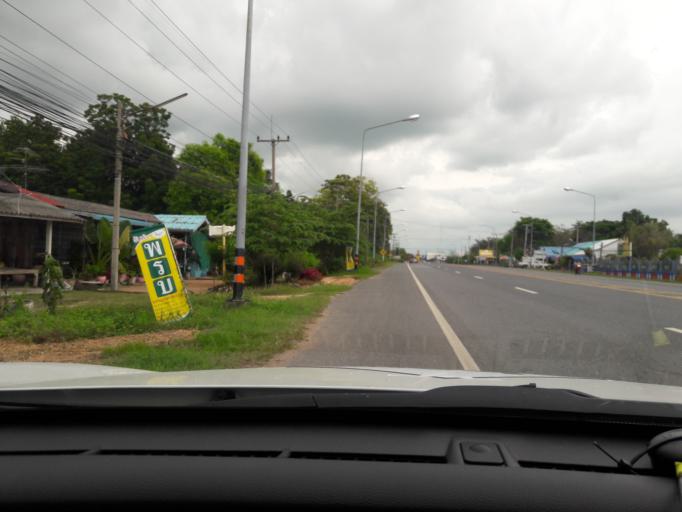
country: TH
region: Nakhon Sawan
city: Tak Fa
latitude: 15.3500
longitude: 100.4926
